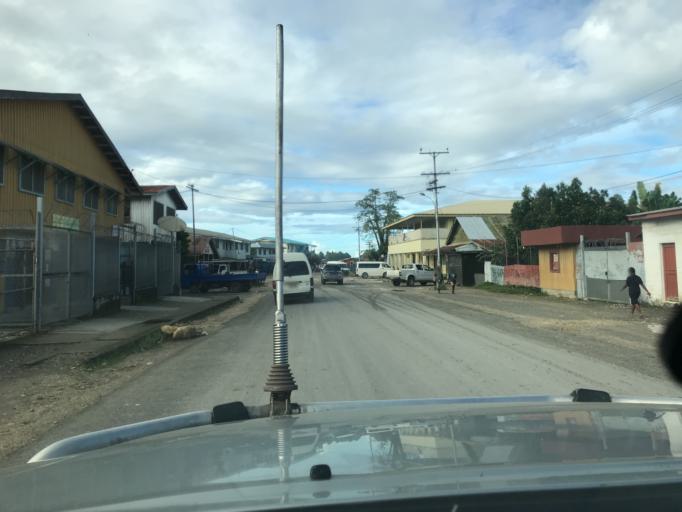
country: SB
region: Malaita
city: Auki
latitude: -8.7716
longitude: 160.6972
